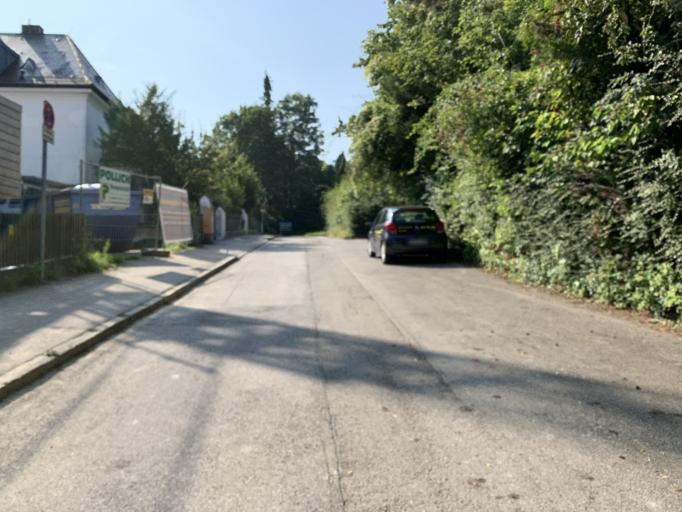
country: DE
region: Bavaria
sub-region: Upper Bavaria
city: Freising
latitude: 48.3969
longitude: 11.7344
